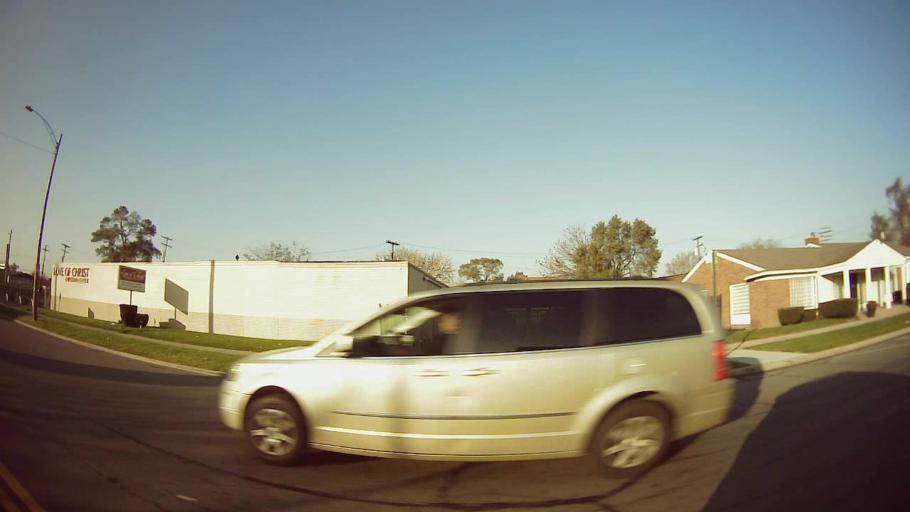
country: US
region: Michigan
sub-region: Oakland County
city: Oak Park
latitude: 42.4327
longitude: -83.1610
